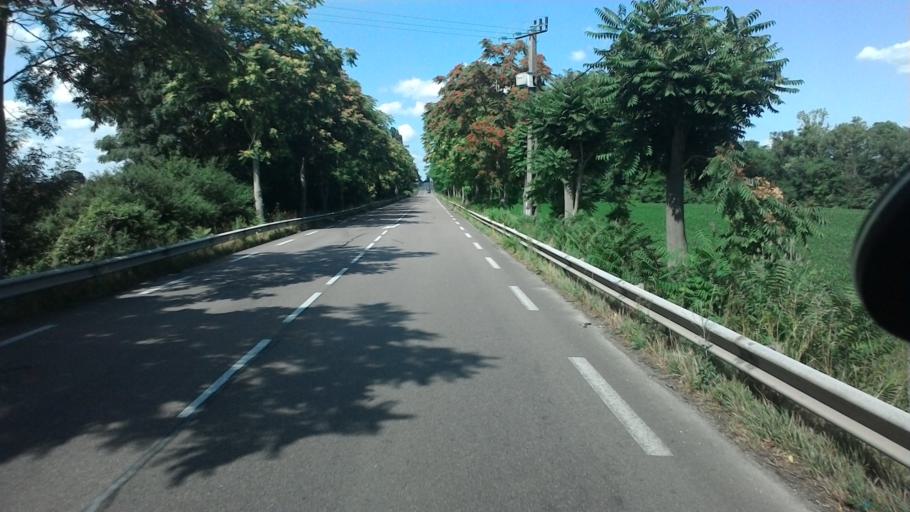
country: FR
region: Bourgogne
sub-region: Departement de la Cote-d'Or
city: Seurre
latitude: 46.9414
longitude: 5.1514
